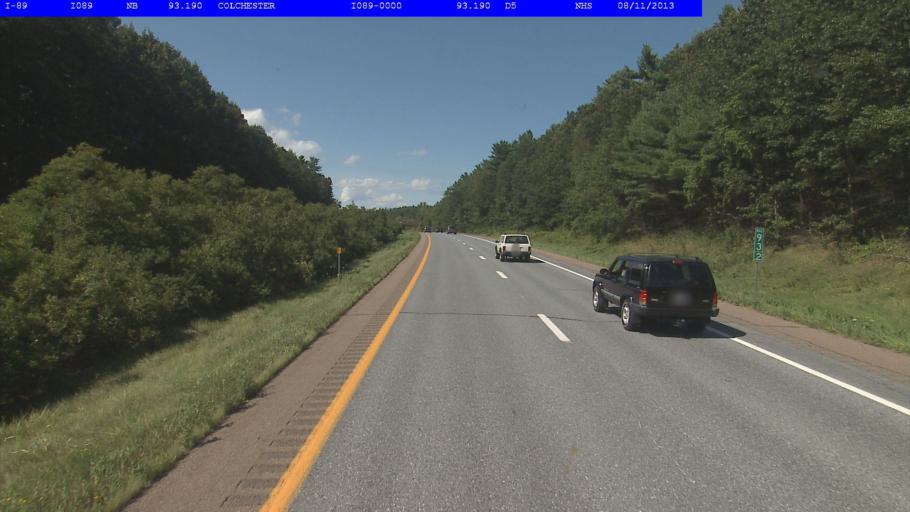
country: US
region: Vermont
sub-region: Chittenden County
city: Winooski
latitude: 44.5268
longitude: -73.1936
